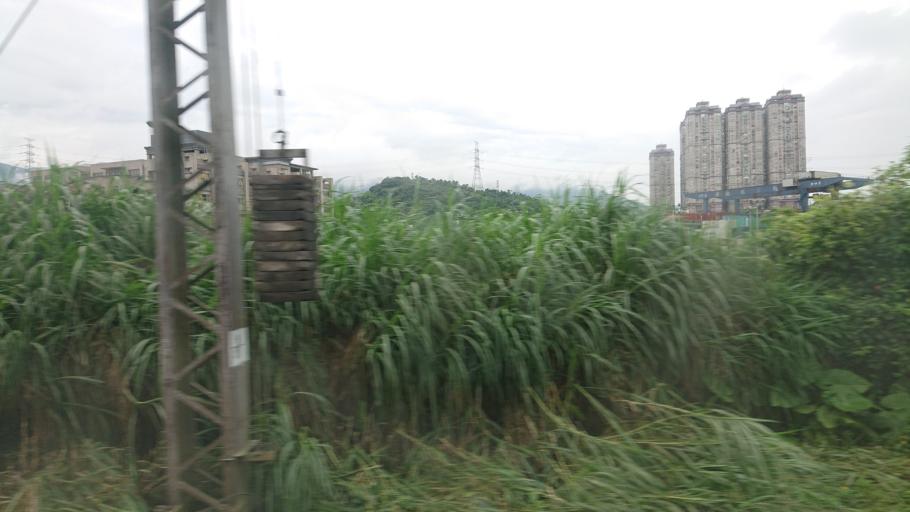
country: TW
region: Taiwan
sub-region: Keelung
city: Keelung
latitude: 25.0792
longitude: 121.6874
